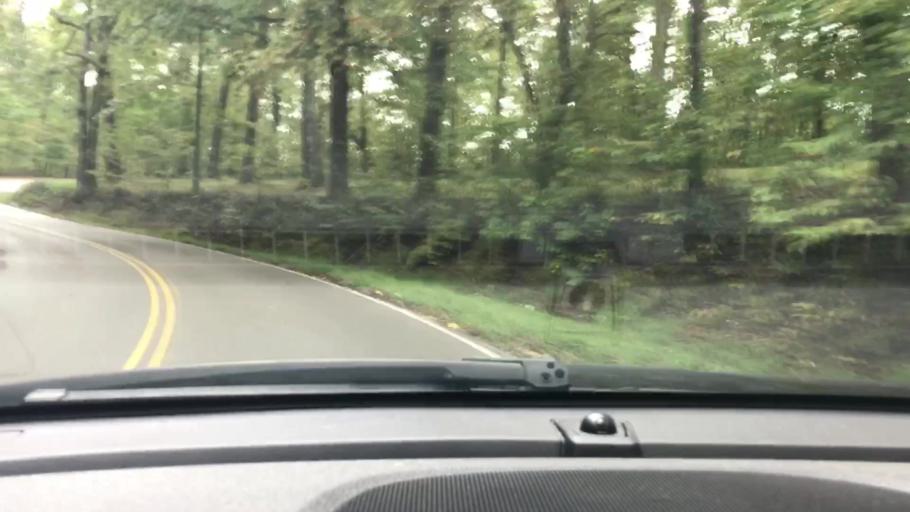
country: US
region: Tennessee
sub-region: Cheatham County
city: Kingston Springs
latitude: 36.1021
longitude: -87.1357
